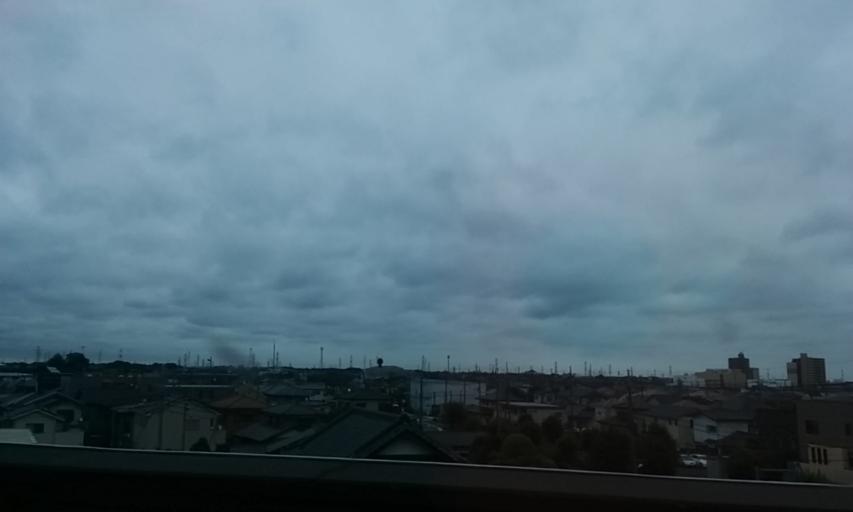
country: JP
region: Saitama
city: Shiraoka
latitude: 36.0244
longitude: 139.6571
